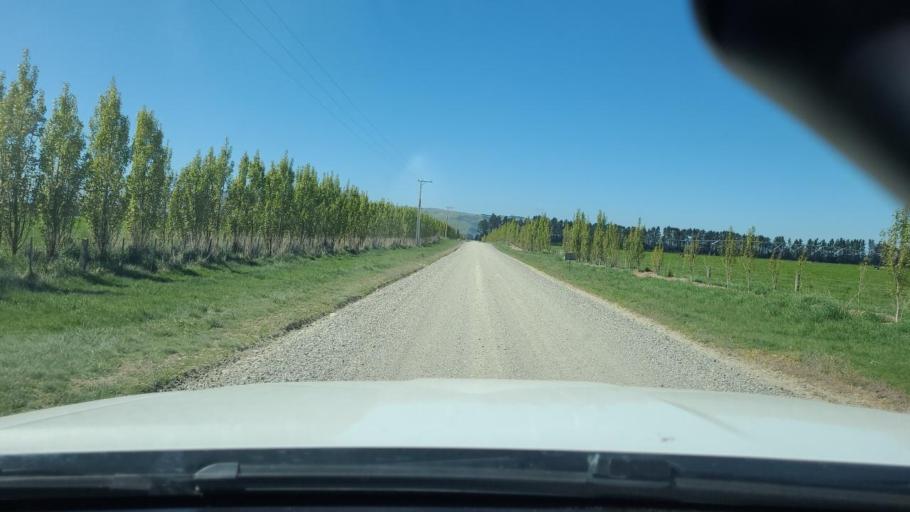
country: NZ
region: Southland
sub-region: Gore District
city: Gore
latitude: -45.7919
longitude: 168.7293
